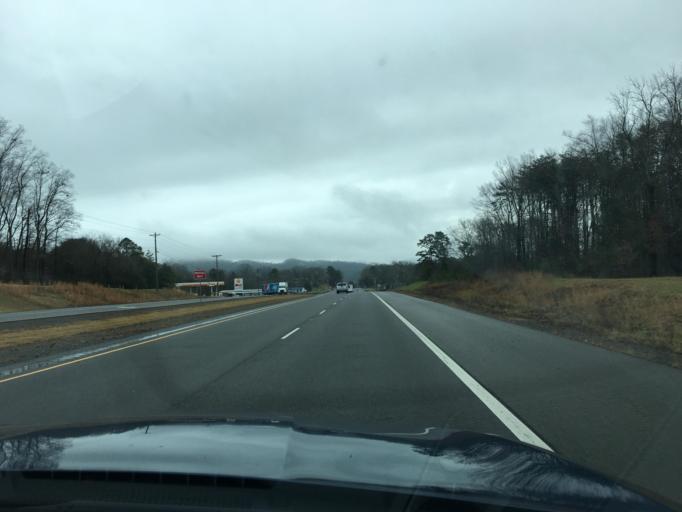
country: US
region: Tennessee
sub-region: McMinn County
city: Etowah
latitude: 35.3410
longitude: -84.5352
